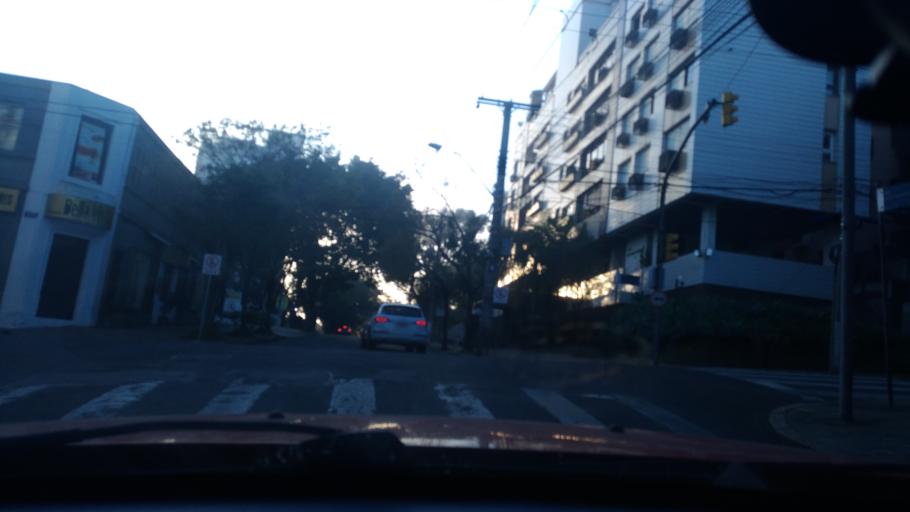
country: BR
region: Rio Grande do Sul
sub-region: Porto Alegre
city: Porto Alegre
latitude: -30.0274
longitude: -51.1949
